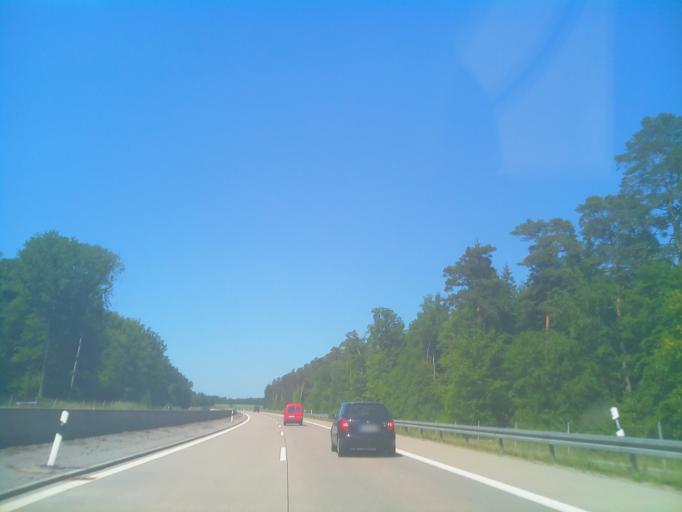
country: DE
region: Bavaria
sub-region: Regierungsbezirk Unterfranken
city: Strahlungen
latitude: 50.2801
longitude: 10.2585
